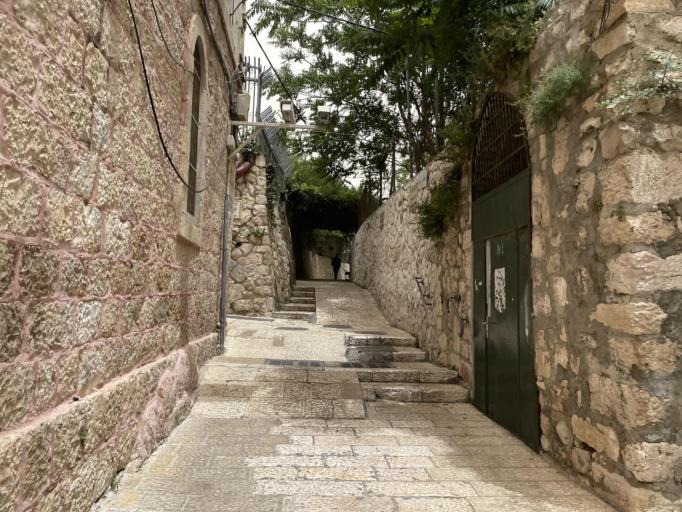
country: PS
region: West Bank
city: East Jerusalem
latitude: 31.7822
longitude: 35.2331
